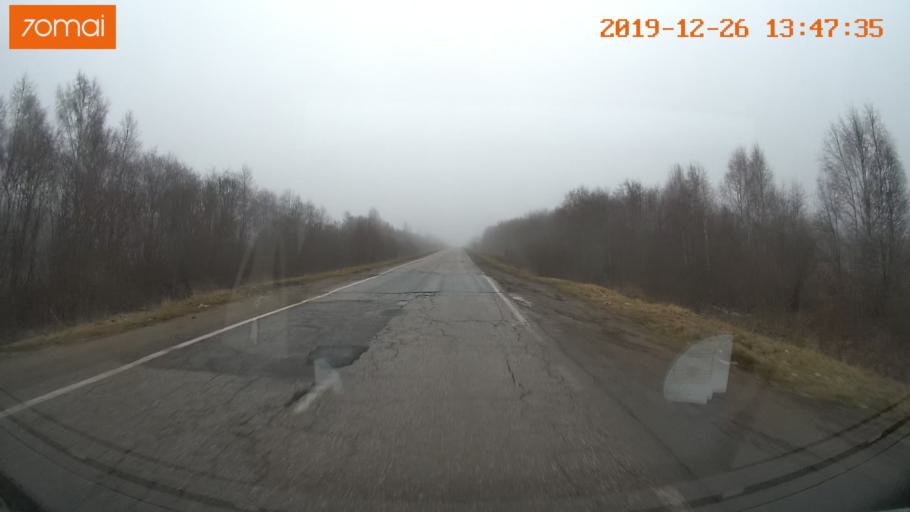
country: RU
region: Vologda
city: Sheksna
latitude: 58.6837
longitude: 38.5358
